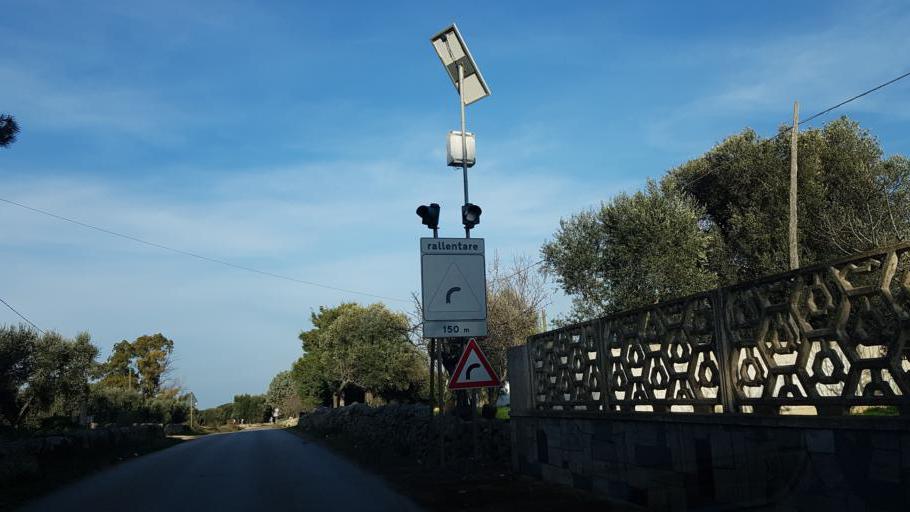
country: IT
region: Apulia
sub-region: Provincia di Brindisi
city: Carovigno
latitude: 40.7044
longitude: 17.6836
